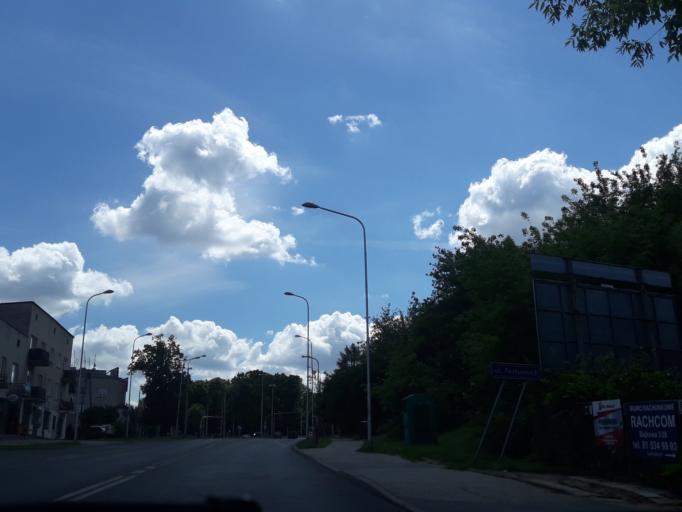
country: PL
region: Lublin Voivodeship
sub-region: Powiat lubelski
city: Lublin
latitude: 51.2526
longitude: 22.5231
